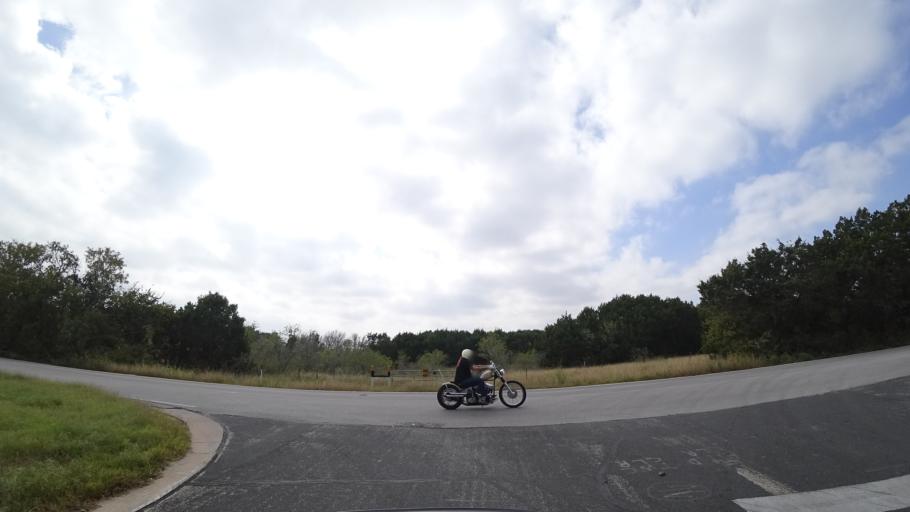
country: US
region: Texas
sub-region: Travis County
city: Shady Hollow
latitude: 30.1924
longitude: -97.8361
